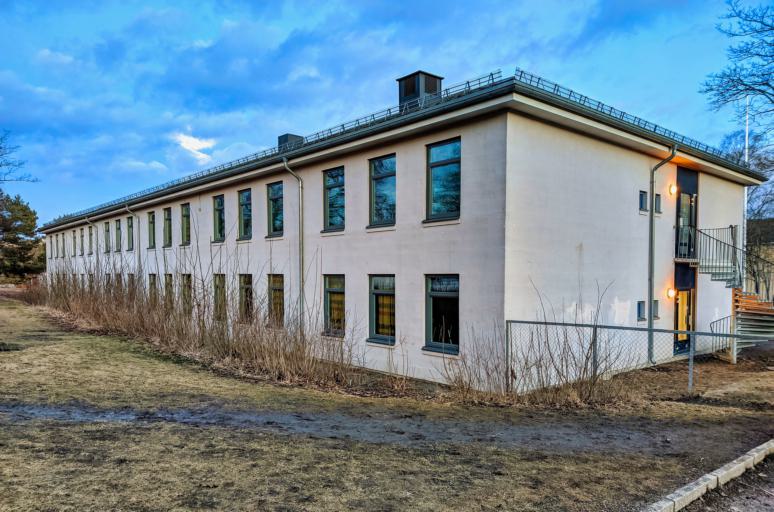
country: NO
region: Oslo
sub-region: Oslo
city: Oslo
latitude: 59.9148
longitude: 10.8221
